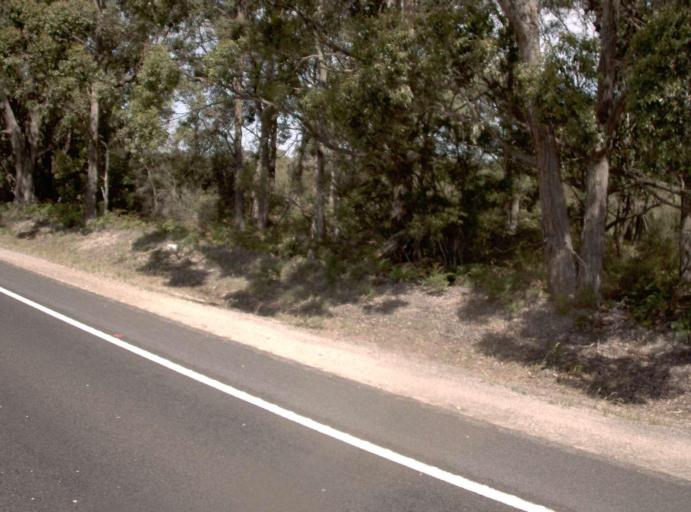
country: AU
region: Victoria
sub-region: East Gippsland
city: Bairnsdale
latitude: -37.8755
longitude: 147.4473
